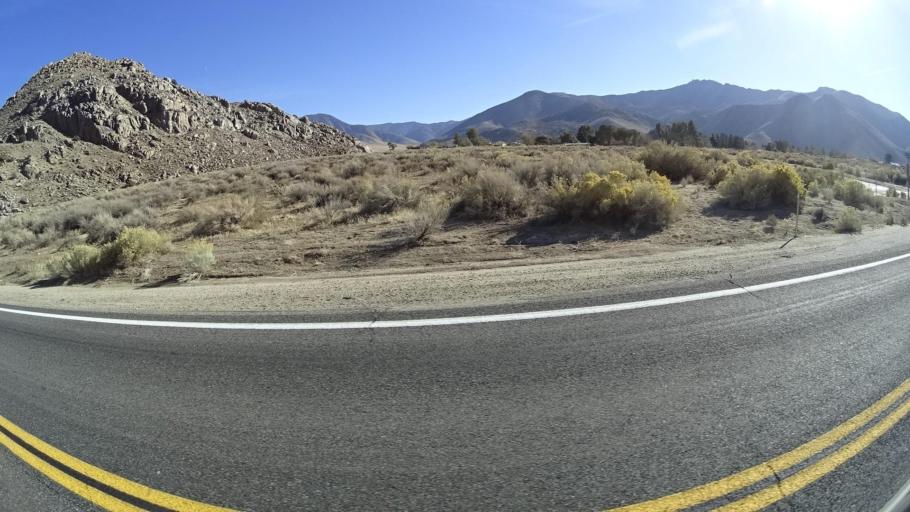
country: US
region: California
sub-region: Kern County
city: Weldon
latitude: 35.6949
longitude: -118.2188
